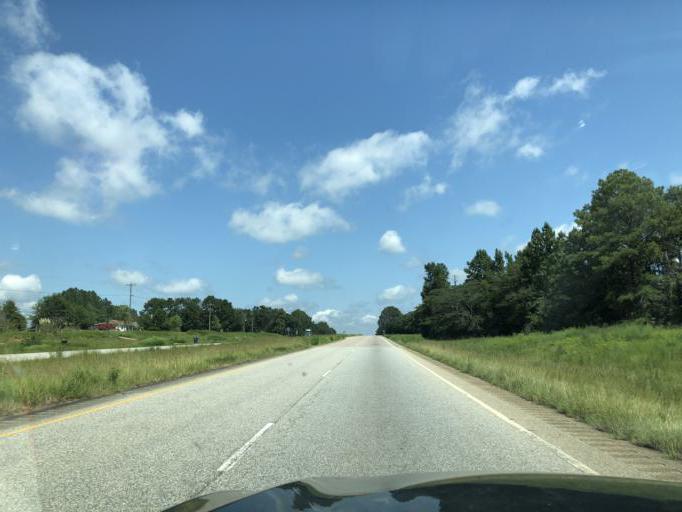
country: US
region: Alabama
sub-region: Henry County
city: Abbeville
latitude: 31.6993
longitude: -85.2778
